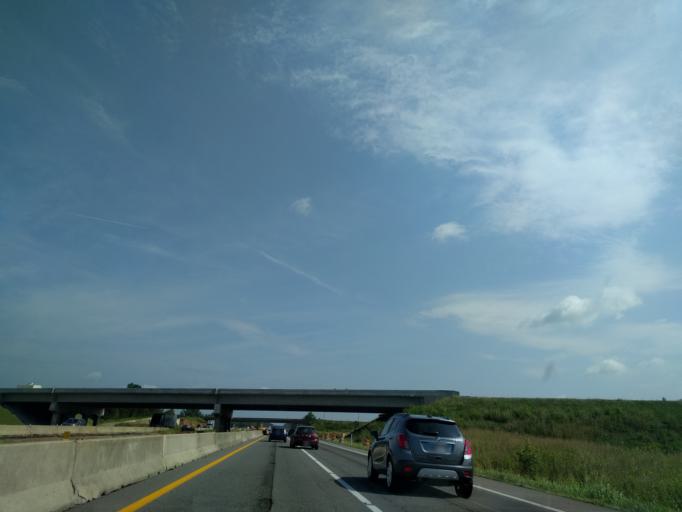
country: US
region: Tennessee
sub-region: Sumner County
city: Portland
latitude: 36.6296
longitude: -86.5740
